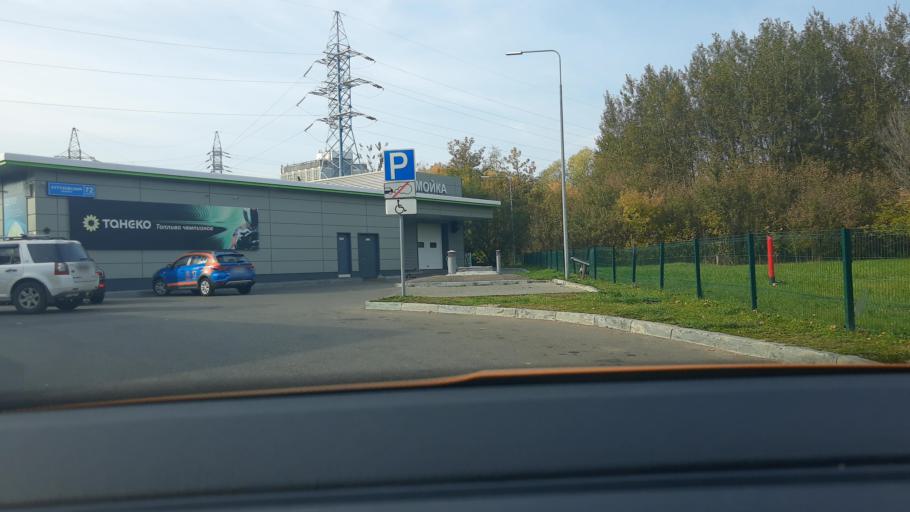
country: RU
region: Moscow
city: Davydkovo
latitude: 55.7272
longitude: 37.4628
